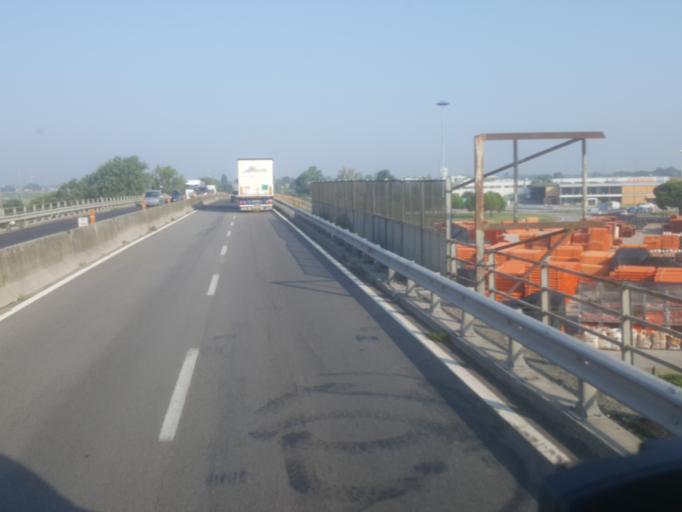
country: IT
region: Emilia-Romagna
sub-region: Provincia di Ravenna
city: Fornace Zarattini
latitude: 44.4213
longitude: 12.1638
